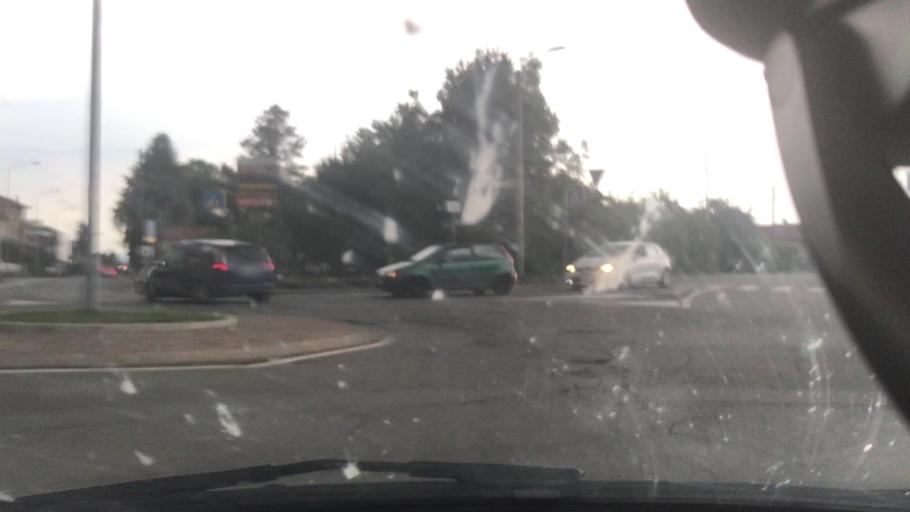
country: IT
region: Piedmont
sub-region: Provincia di Biella
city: Biella
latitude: 45.5693
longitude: 8.0725
